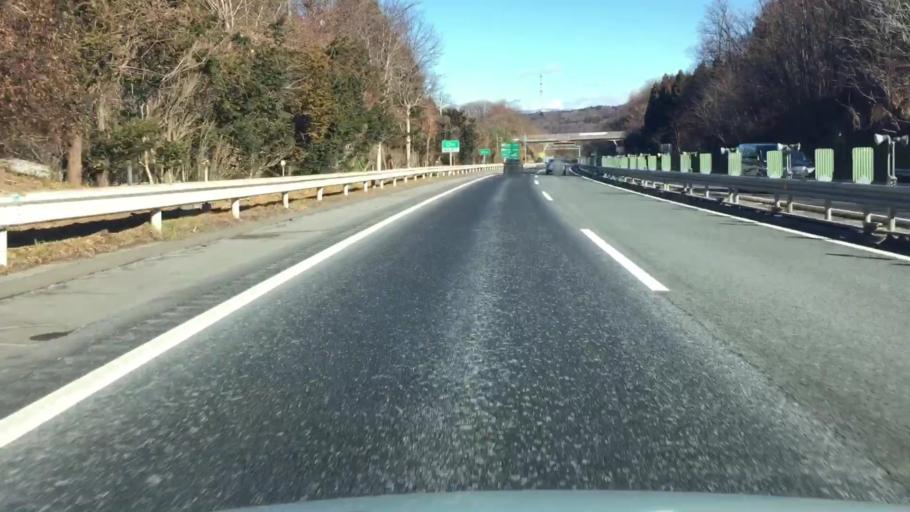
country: JP
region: Gunma
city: Numata
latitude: 36.5527
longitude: 139.0547
